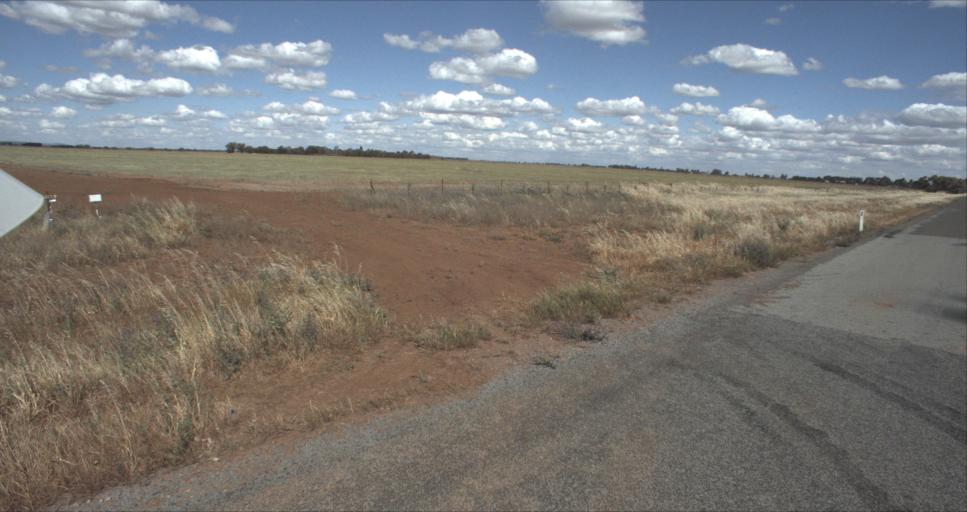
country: AU
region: New South Wales
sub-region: Leeton
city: Leeton
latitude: -34.4652
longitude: 146.2520
